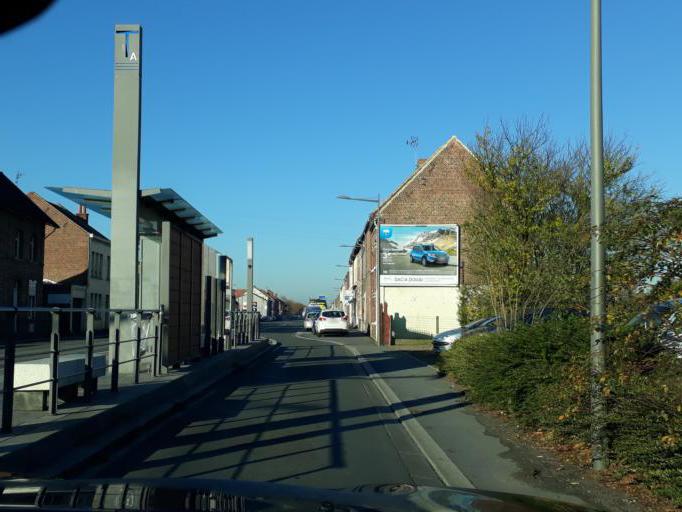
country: FR
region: Nord-Pas-de-Calais
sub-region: Departement du Nord
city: Guesnain
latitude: 50.3499
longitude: 3.1376
